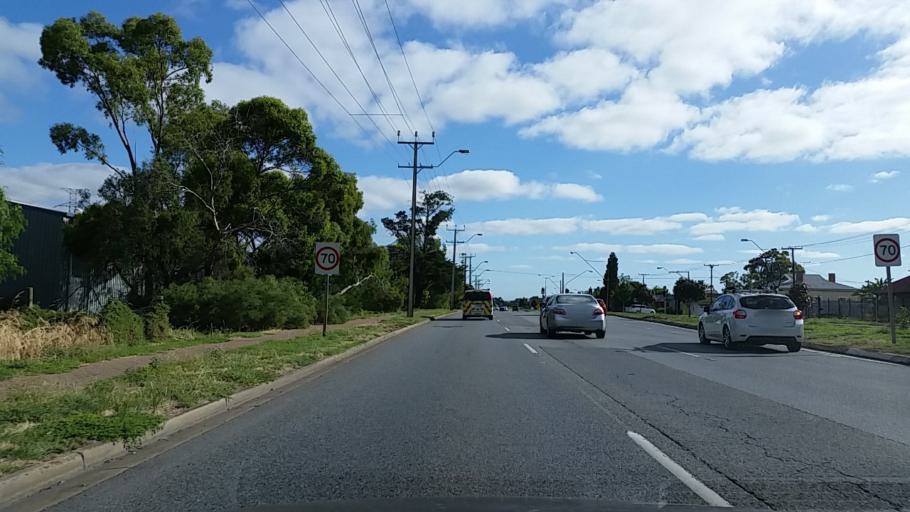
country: AU
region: South Australia
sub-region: Port Adelaide Enfield
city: Enfield
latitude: -34.8332
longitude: 138.6108
